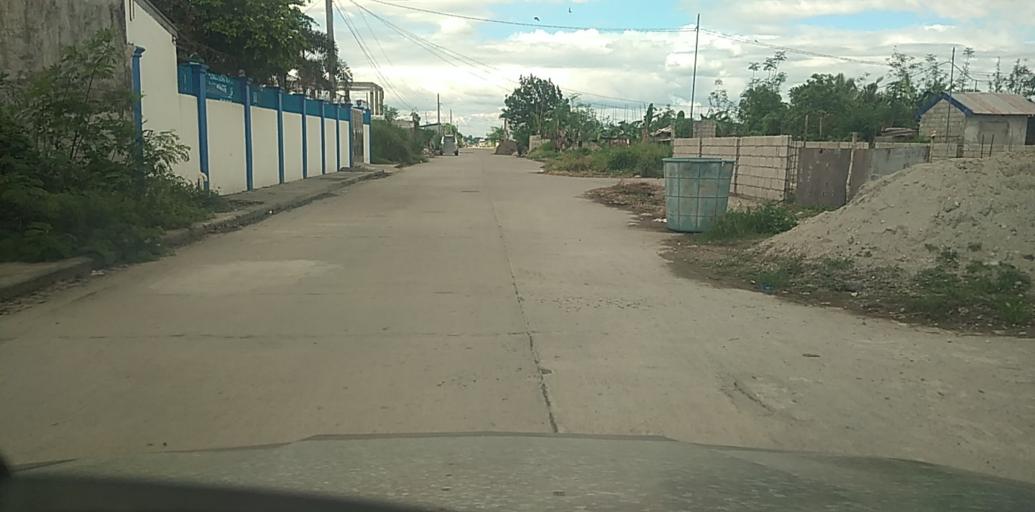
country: PH
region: Central Luzon
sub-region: Province of Pampanga
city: Pandacaqui
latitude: 15.1793
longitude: 120.6673
